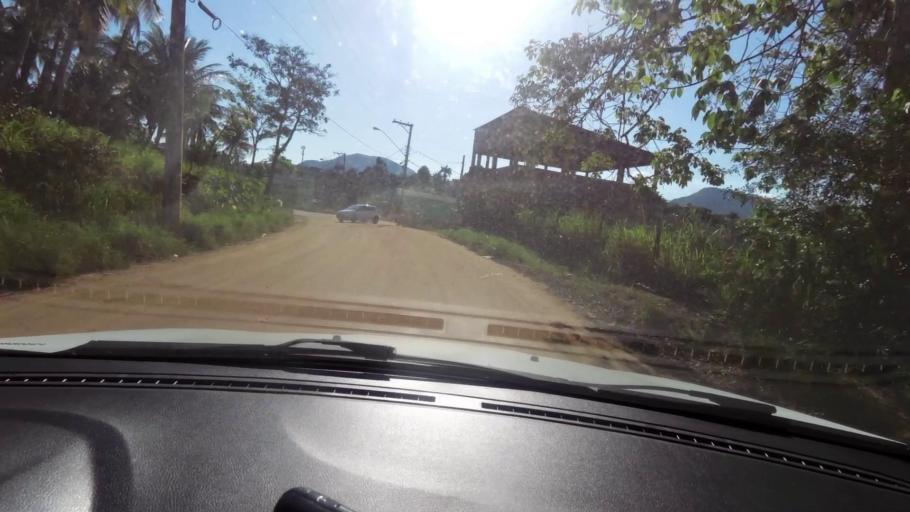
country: BR
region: Espirito Santo
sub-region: Guarapari
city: Guarapari
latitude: -20.6474
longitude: -40.5093
